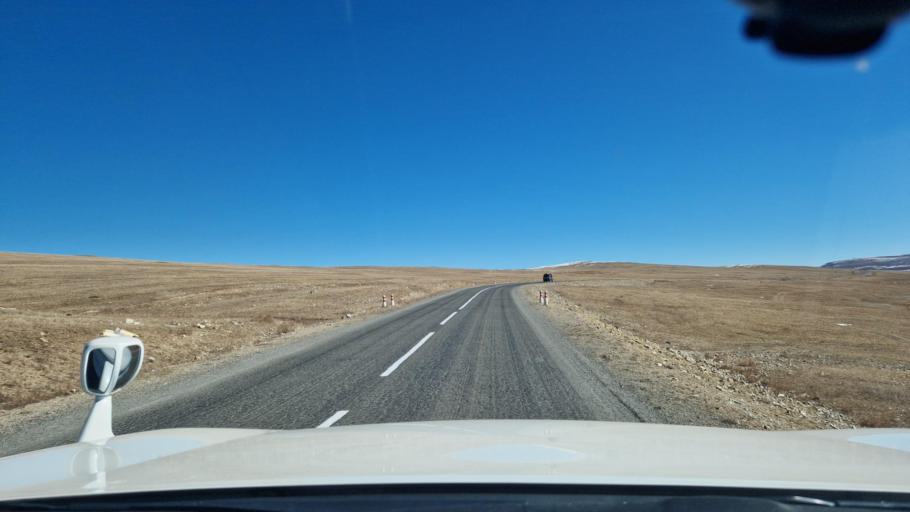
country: MN
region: Hentiy
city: Modot
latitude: 47.8057
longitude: 108.7318
